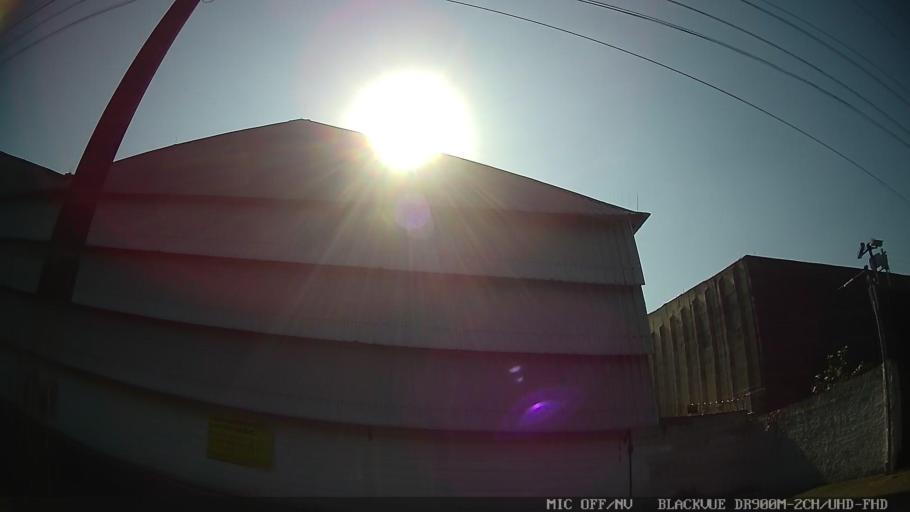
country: BR
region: Sao Paulo
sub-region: Guaruja
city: Guaruja
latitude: -24.0024
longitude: -46.2943
